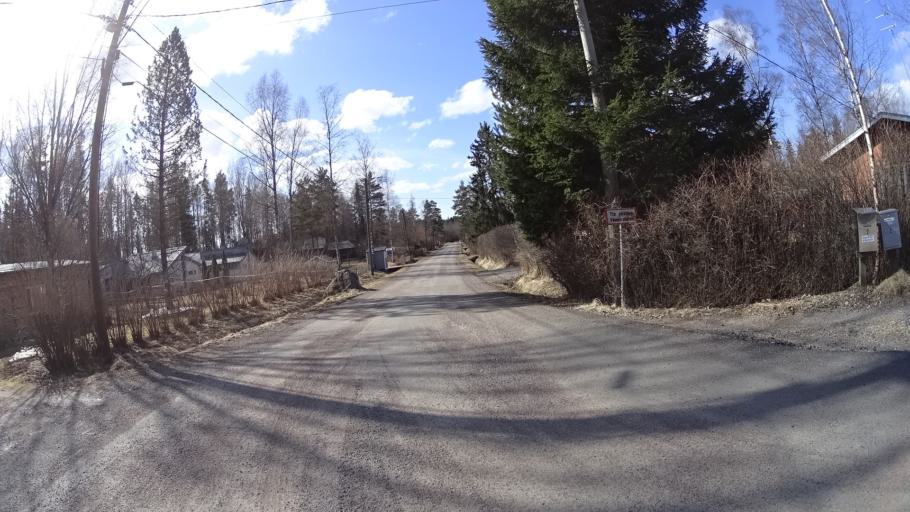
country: FI
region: Uusimaa
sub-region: Helsinki
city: Kauniainen
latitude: 60.2788
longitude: 24.7295
